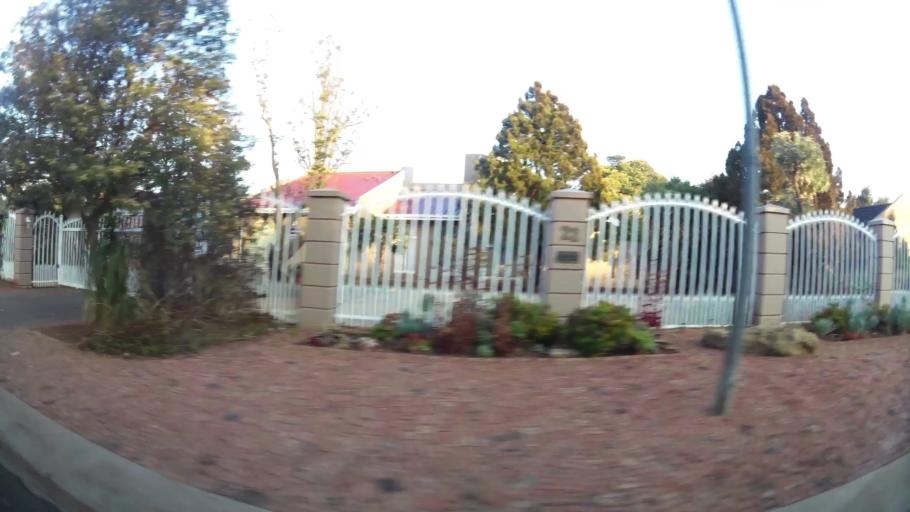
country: ZA
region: Orange Free State
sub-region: Mangaung Metropolitan Municipality
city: Bloemfontein
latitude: -29.1041
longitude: 26.1584
